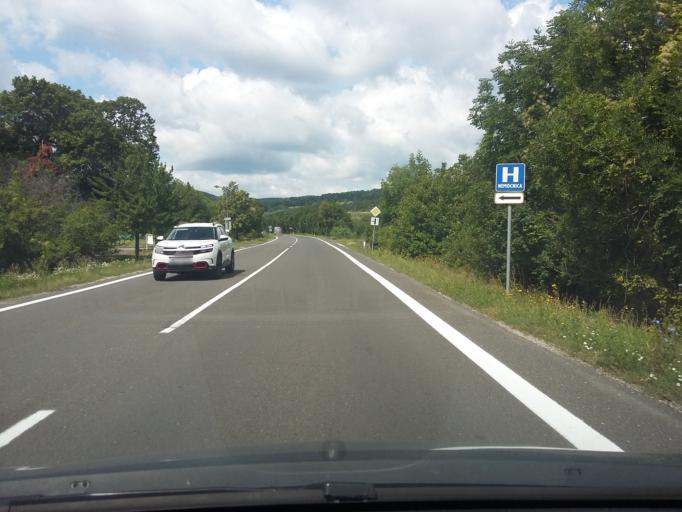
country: SK
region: Bratislavsky
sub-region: Okres Pezinok
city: Pezinok
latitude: 48.3165
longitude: 17.2578
